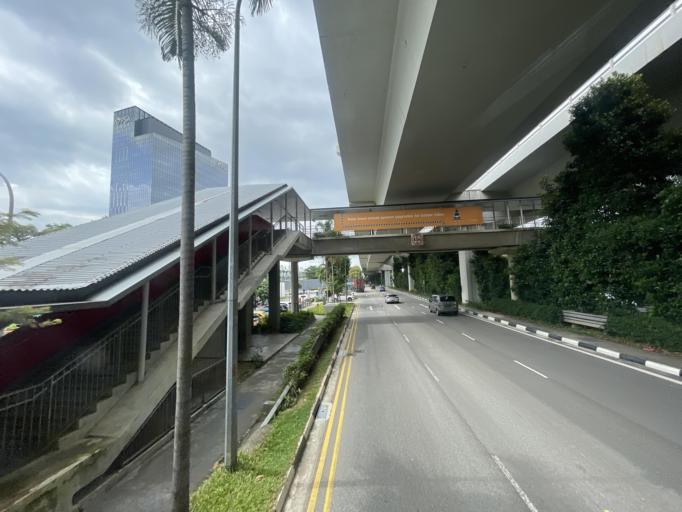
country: SG
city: Singapore
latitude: 1.2762
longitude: 103.7918
